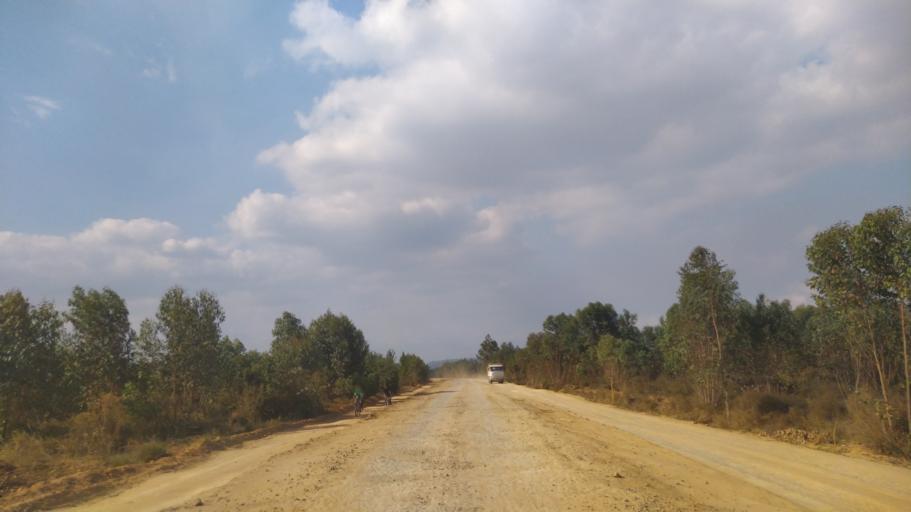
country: MG
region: Alaotra Mangoro
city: Moramanga
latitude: -18.6483
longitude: 48.2745
